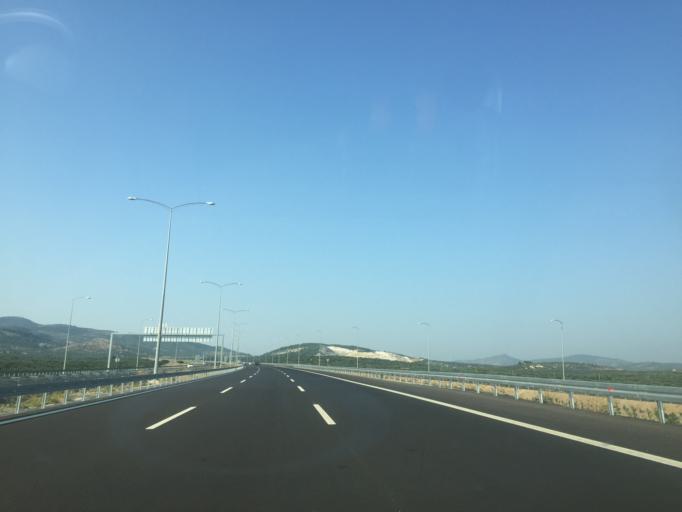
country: TR
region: Manisa
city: Zeytinliova
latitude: 38.9679
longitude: 27.7292
